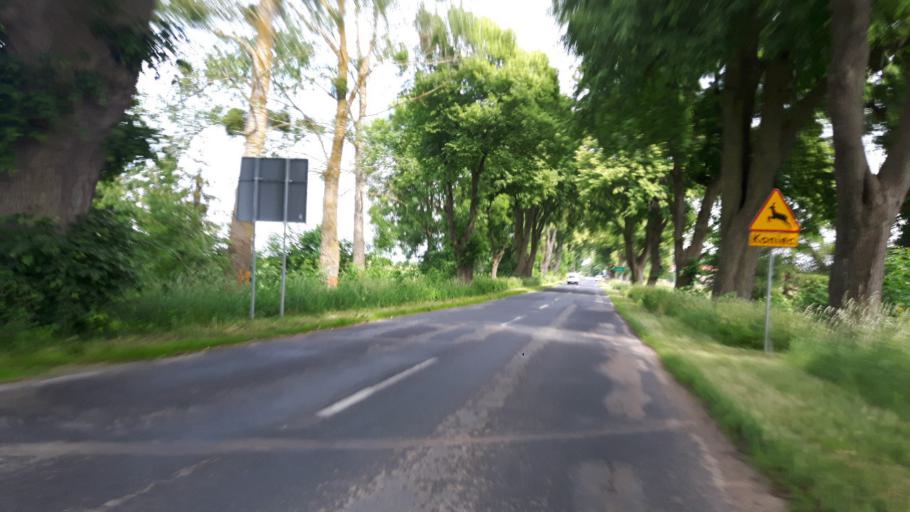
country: PL
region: Warmian-Masurian Voivodeship
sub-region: Powiat braniewski
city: Braniewo
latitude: 54.3641
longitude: 19.7641
